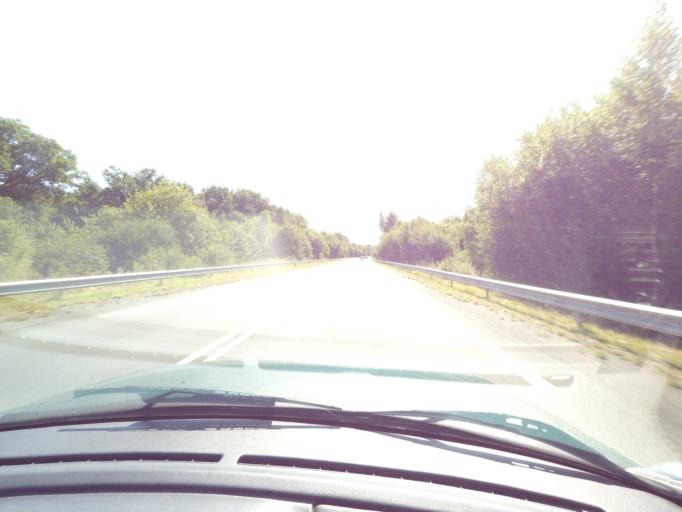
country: FR
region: Limousin
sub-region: Departement de la Haute-Vienne
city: Chaptelat
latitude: 45.8975
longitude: 1.2429
